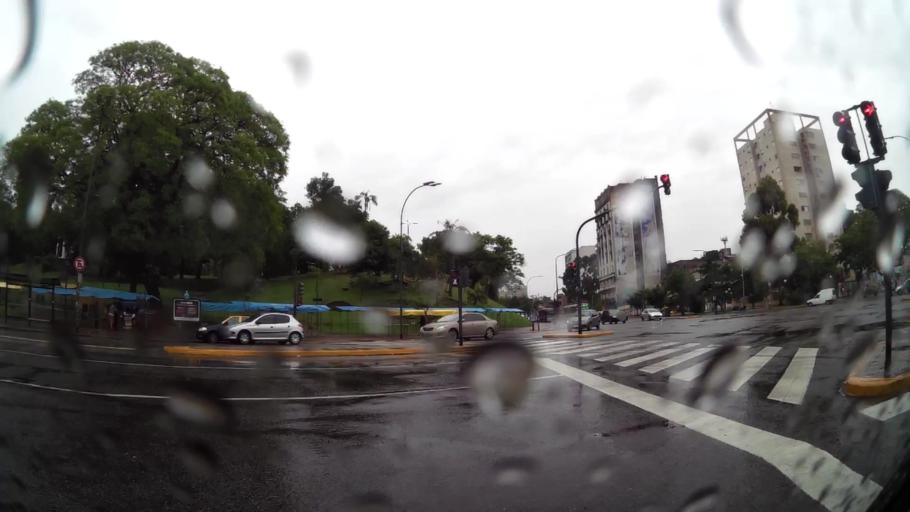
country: AR
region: Buenos Aires F.D.
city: Buenos Aires
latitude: -34.6274
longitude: -58.3682
